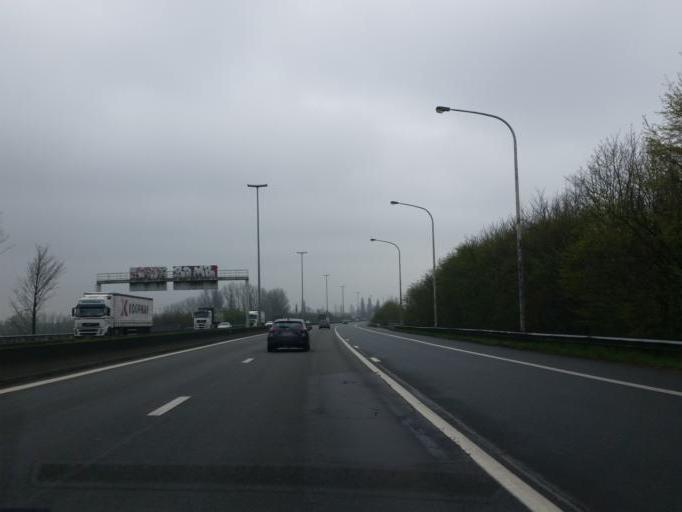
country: BE
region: Flanders
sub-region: Provincie Oost-Vlaanderen
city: Destelbergen
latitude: 51.0456
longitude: 3.8228
